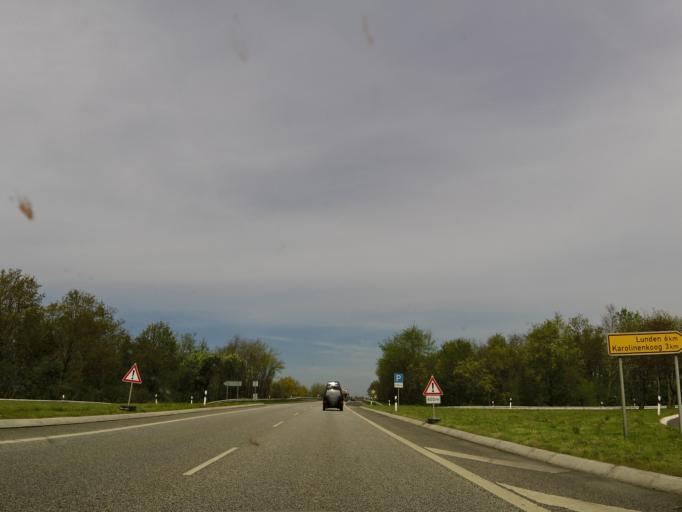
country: DE
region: Schleswig-Holstein
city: Tonning
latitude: 54.3070
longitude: 8.9598
